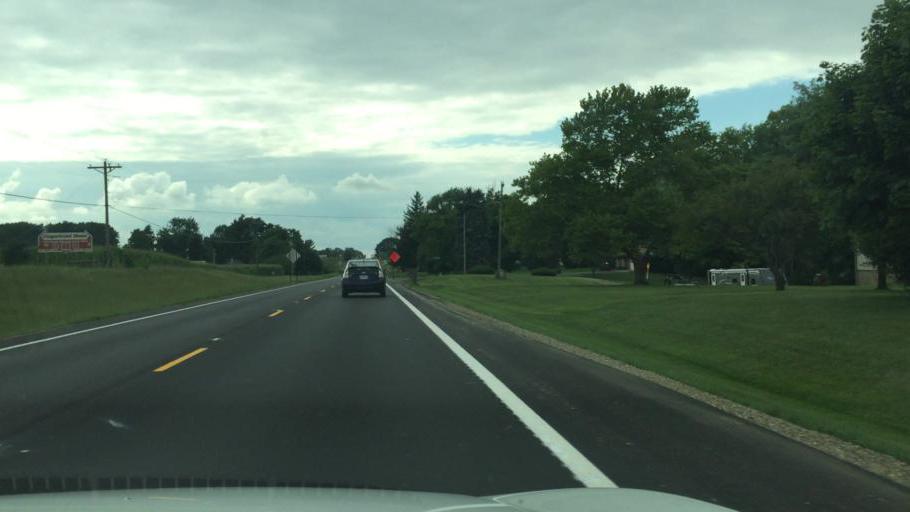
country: US
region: Ohio
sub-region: Champaign County
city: Urbana
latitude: 40.0948
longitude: -83.7033
